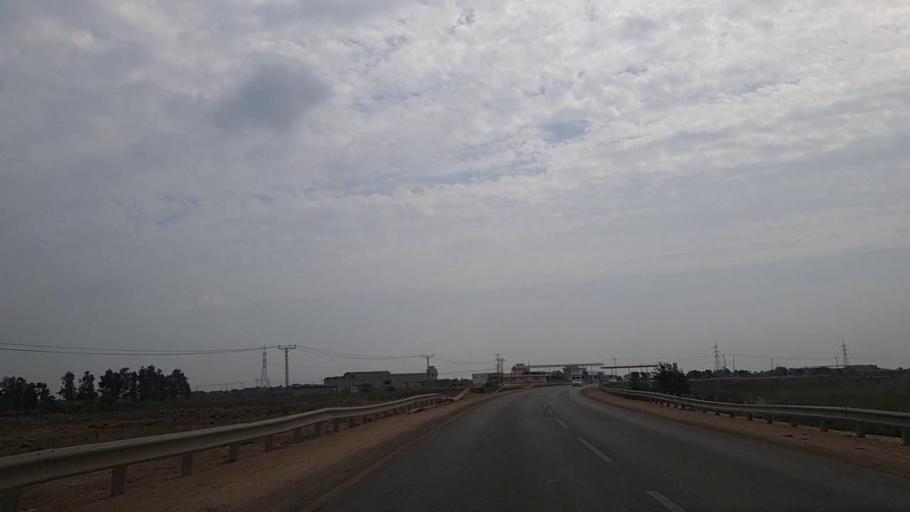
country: PK
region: Sindh
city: Daro Mehar
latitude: 24.6169
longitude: 68.0872
